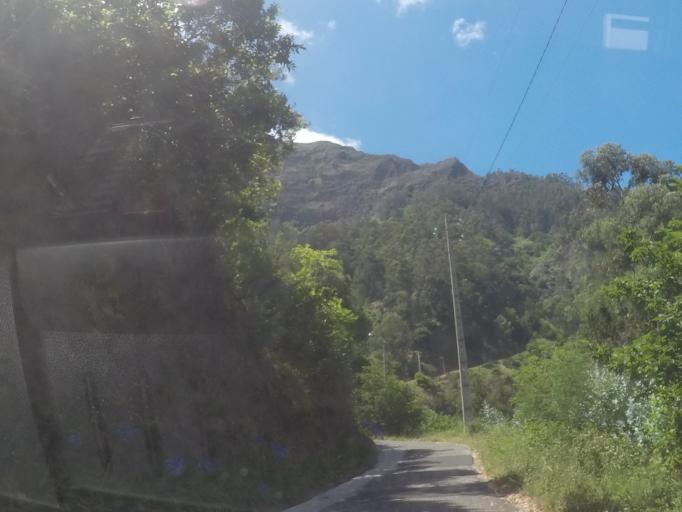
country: PT
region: Madeira
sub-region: Camara de Lobos
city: Curral das Freiras
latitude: 32.7149
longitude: -16.9737
